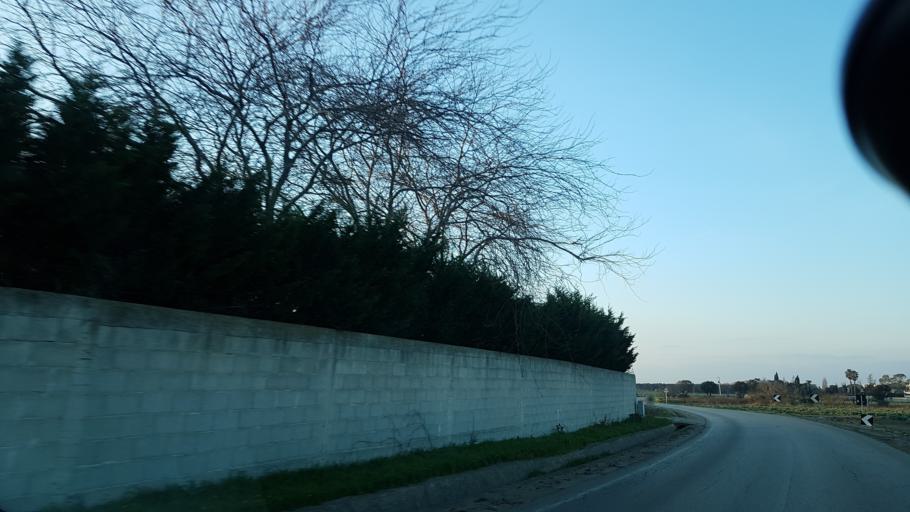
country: IT
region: Apulia
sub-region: Provincia di Brindisi
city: La Rosa
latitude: 40.6041
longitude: 17.9460
